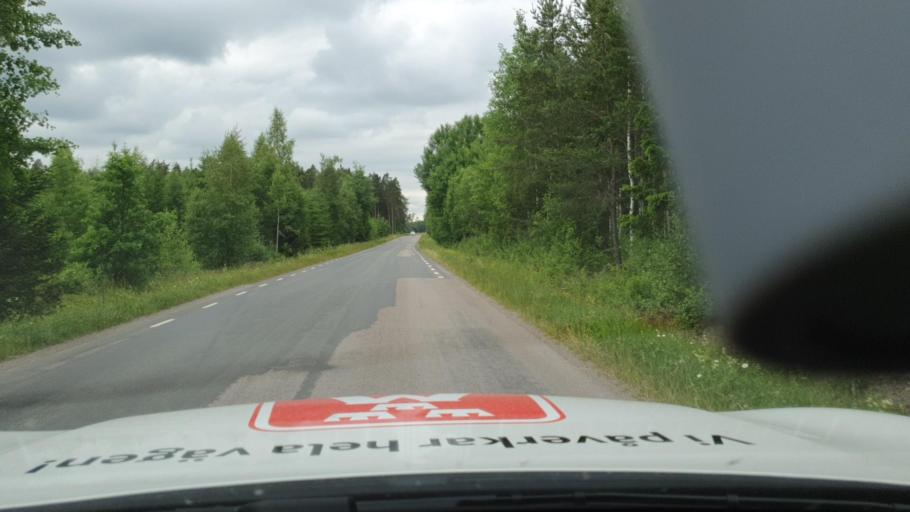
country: SE
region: Vaestra Goetaland
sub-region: Tidaholms Kommun
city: Olofstorp
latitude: 58.3081
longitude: 14.0276
